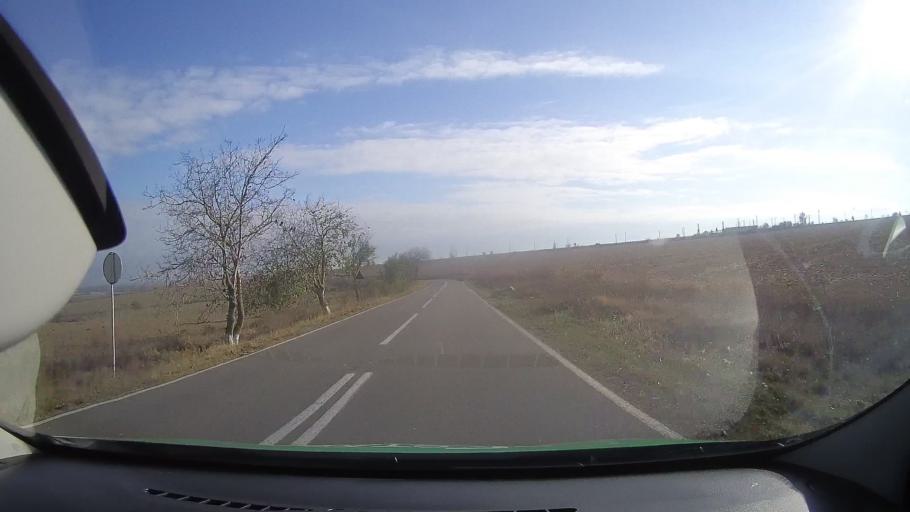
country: RO
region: Tulcea
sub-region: Comuna Mahmudia
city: Mahmudia
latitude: 45.0736
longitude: 29.0836
